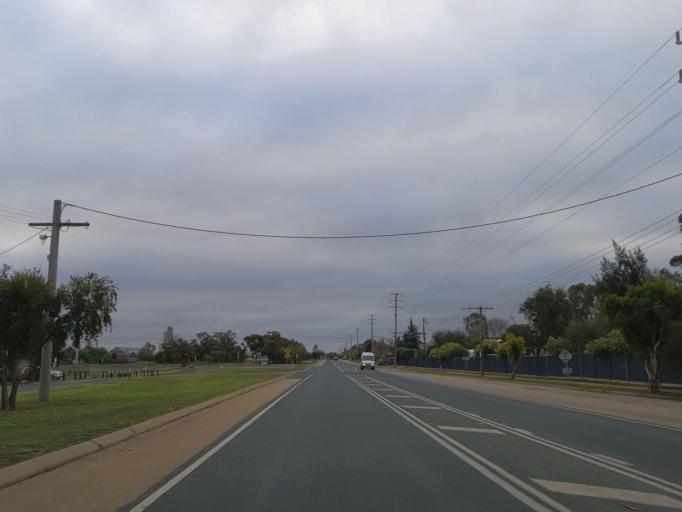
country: AU
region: Victoria
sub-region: Swan Hill
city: Swan Hill
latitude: -35.4628
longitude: 143.6353
